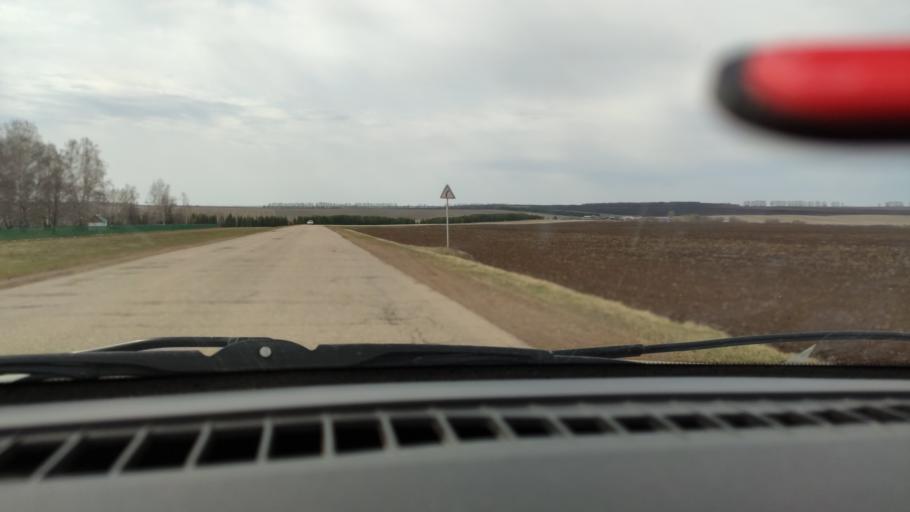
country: RU
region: Bashkortostan
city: Burayevo
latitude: 55.8041
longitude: 55.3628
